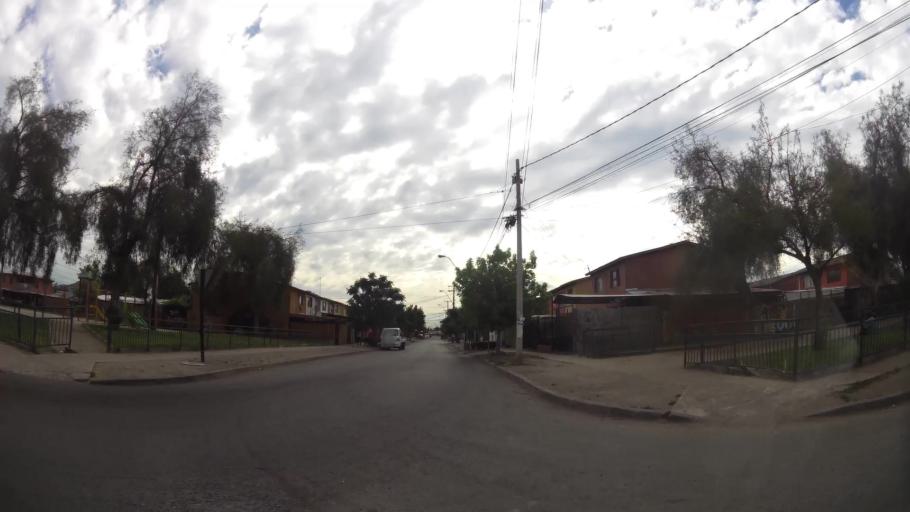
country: CL
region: Santiago Metropolitan
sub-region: Provincia de Cordillera
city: Puente Alto
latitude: -33.6244
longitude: -70.6094
